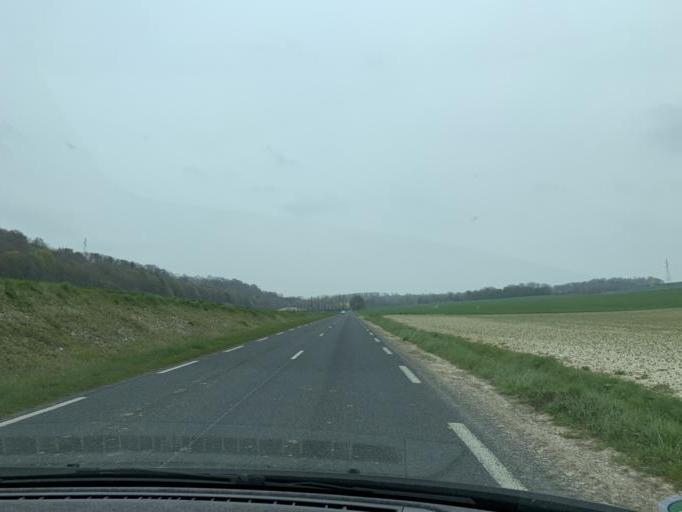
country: FR
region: Haute-Normandie
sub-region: Departement de la Seine-Maritime
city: Londinieres
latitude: 49.8418
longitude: 1.4291
